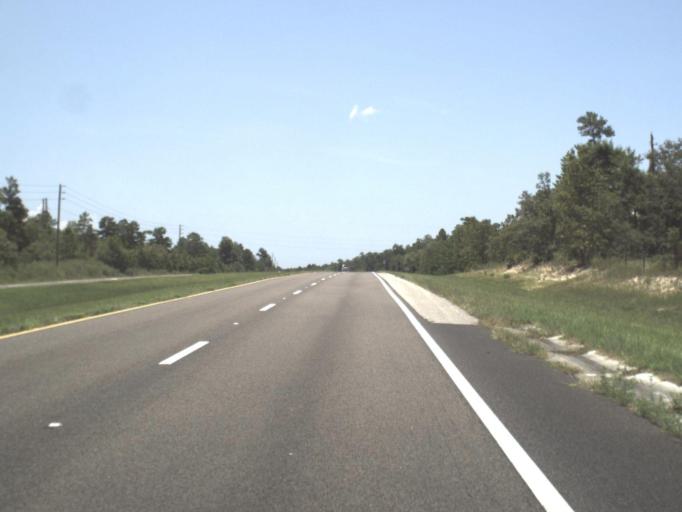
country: US
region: Florida
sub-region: Citrus County
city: Sugarmill Woods
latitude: 28.6992
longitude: -82.5128
